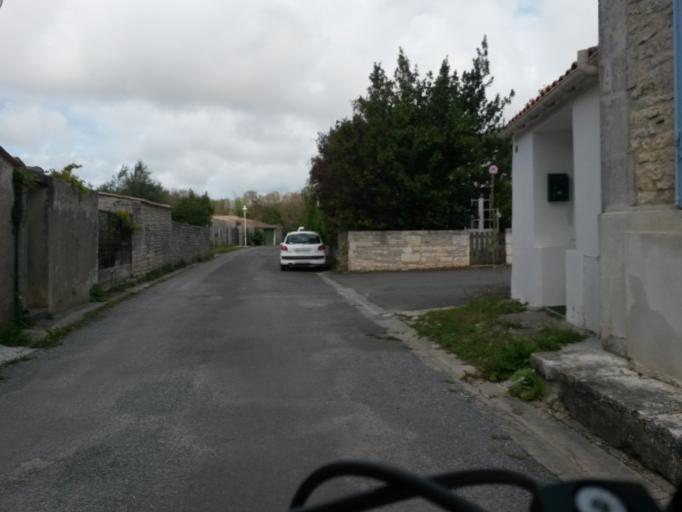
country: FR
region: Poitou-Charentes
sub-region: Departement de la Charente-Maritime
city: Dolus-d'Oleron
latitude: 45.9442
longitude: -1.2888
